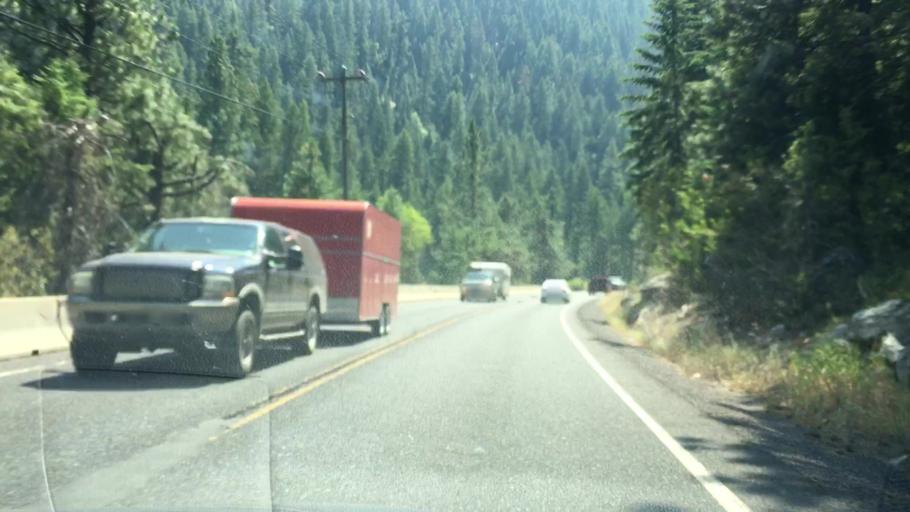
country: US
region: Idaho
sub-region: Valley County
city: McCall
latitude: 45.1315
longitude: -116.2848
